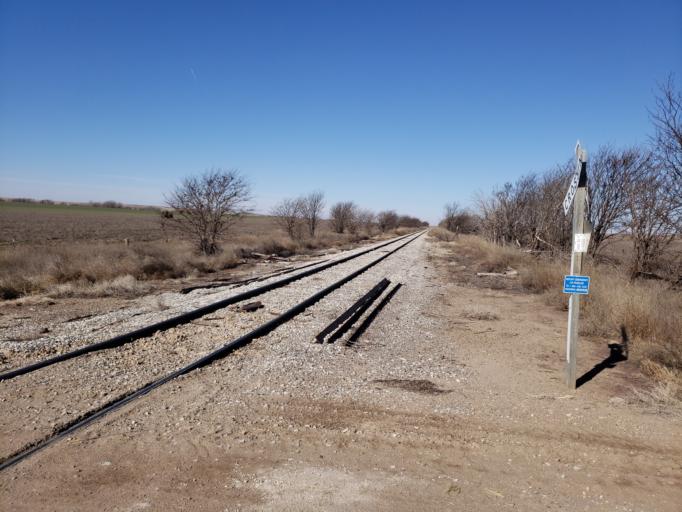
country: US
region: Kansas
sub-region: Ness County
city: Ness City
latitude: 38.4488
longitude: -100.1191
